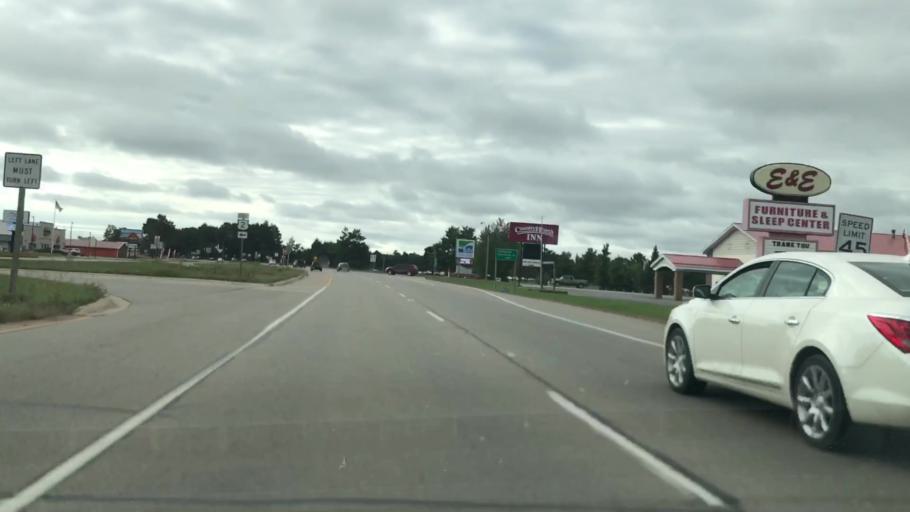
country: US
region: Michigan
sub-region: Delta County
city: Escanaba
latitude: 45.7766
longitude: -87.0835
